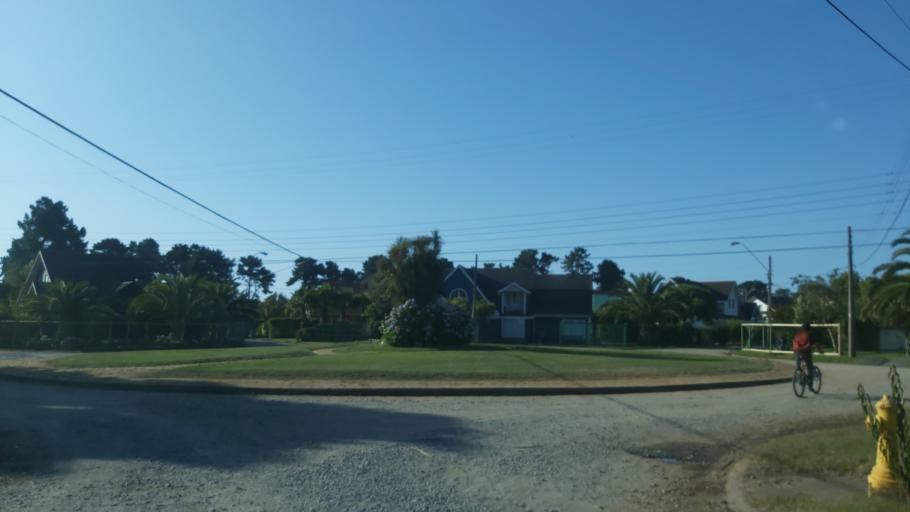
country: CL
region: Biobio
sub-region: Provincia de Concepcion
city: Tome
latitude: -36.5316
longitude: -72.9326
